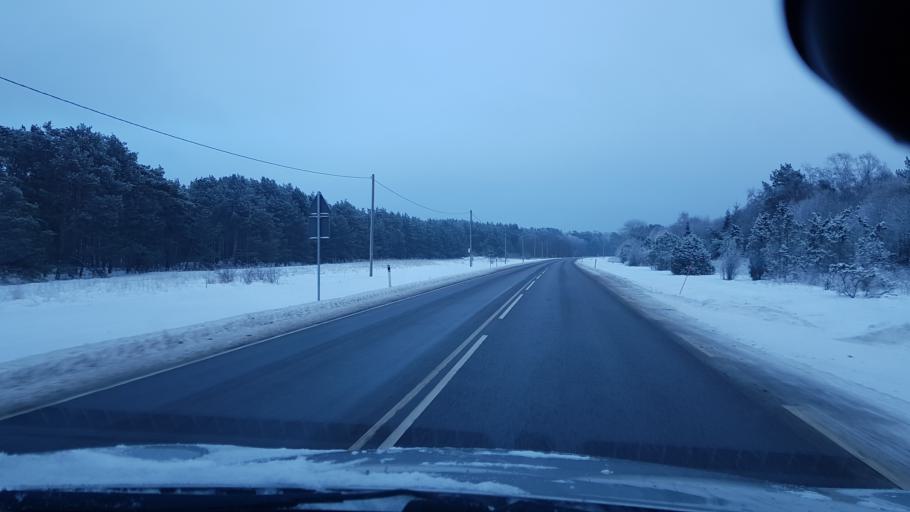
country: EE
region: Harju
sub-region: Paldiski linn
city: Paldiski
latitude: 59.3394
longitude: 24.2082
